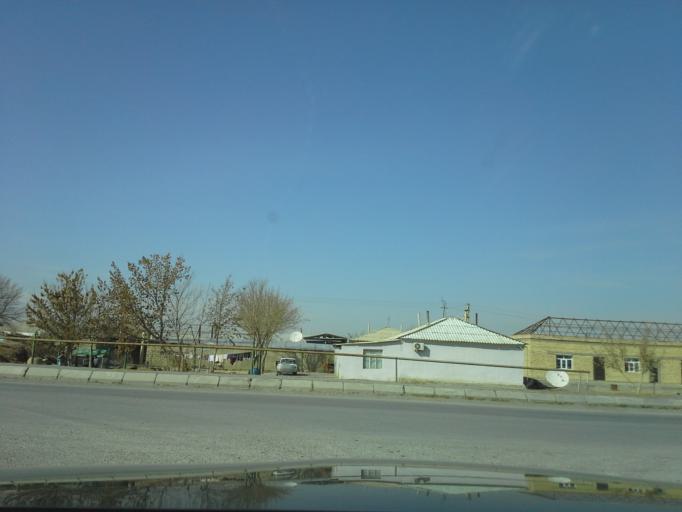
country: TM
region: Ahal
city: Abadan
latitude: 38.1133
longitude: 58.0355
